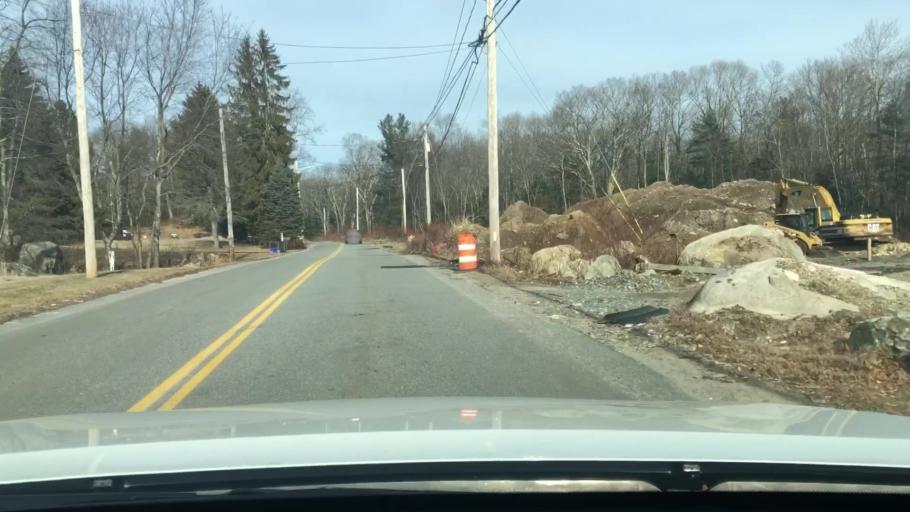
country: US
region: Massachusetts
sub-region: Worcester County
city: Milford
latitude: 42.1245
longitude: -71.4944
